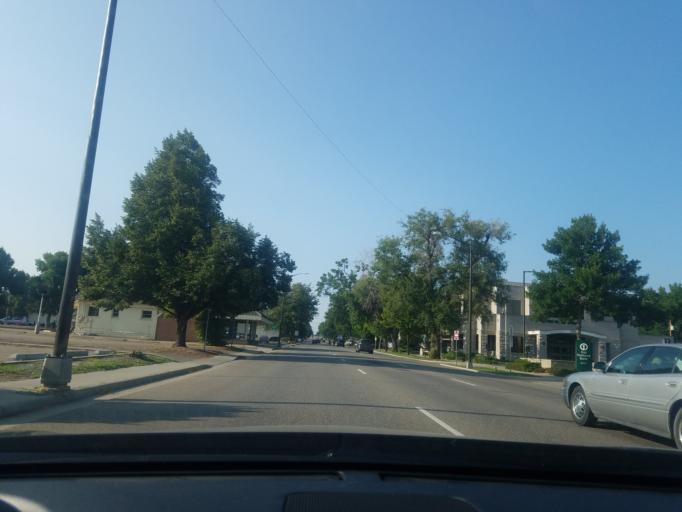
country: US
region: Colorado
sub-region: Larimer County
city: Loveland
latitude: 40.3989
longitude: -105.0732
